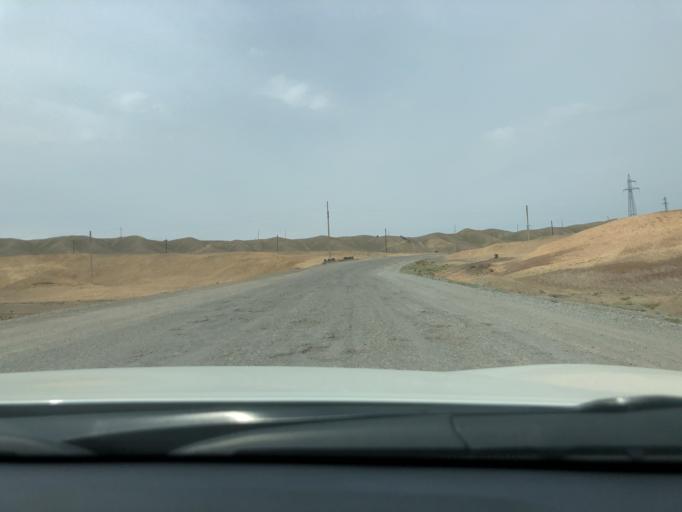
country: TJ
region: Viloyati Sughd
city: Kim
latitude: 40.2128
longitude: 70.4748
